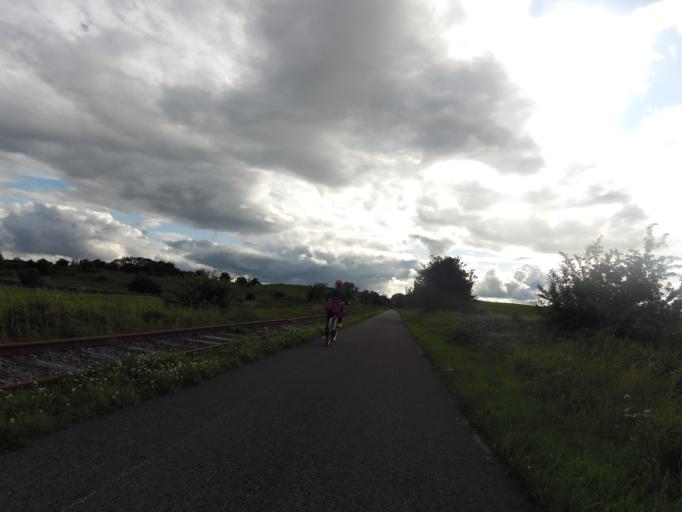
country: IE
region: Leinster
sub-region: An Iarmhi
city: Kilbeggan
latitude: 53.4694
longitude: -7.4948
